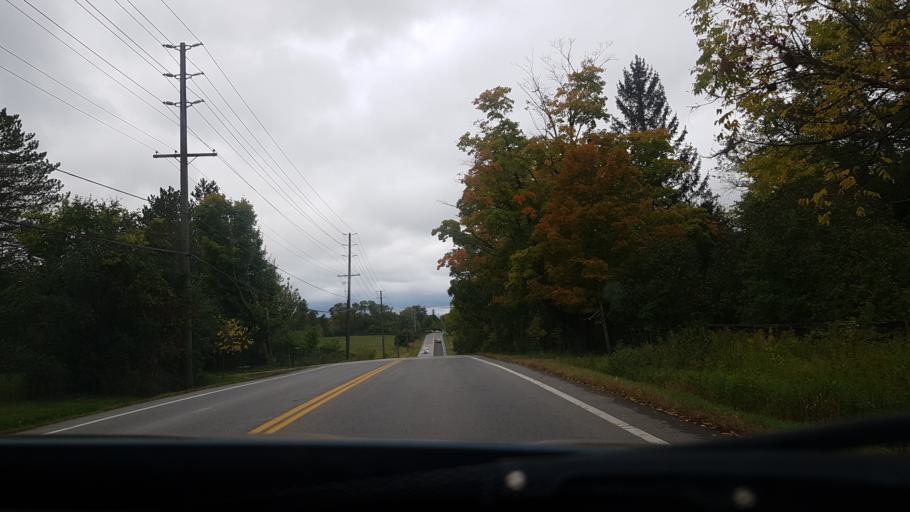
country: CA
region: Ontario
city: Newmarket
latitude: 44.0596
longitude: -79.3732
